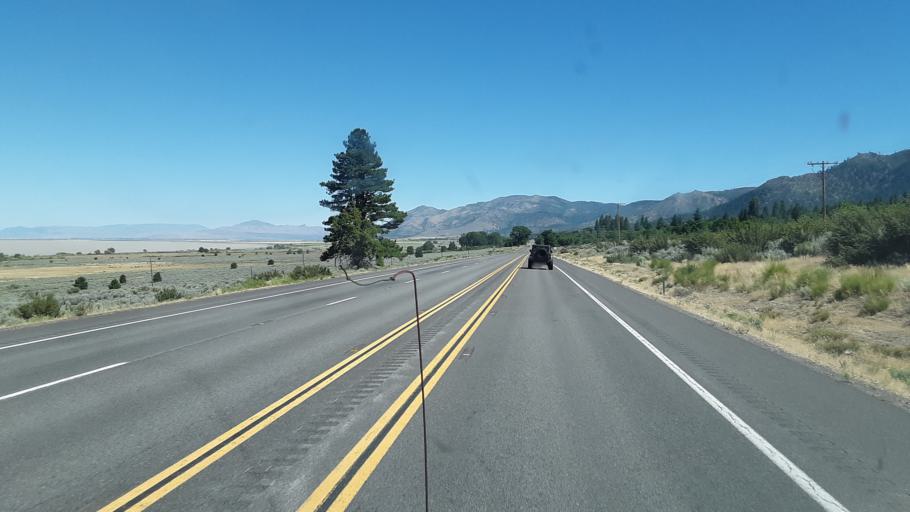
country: US
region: California
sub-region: Lassen County
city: Janesville
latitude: 40.2167
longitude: -120.4276
